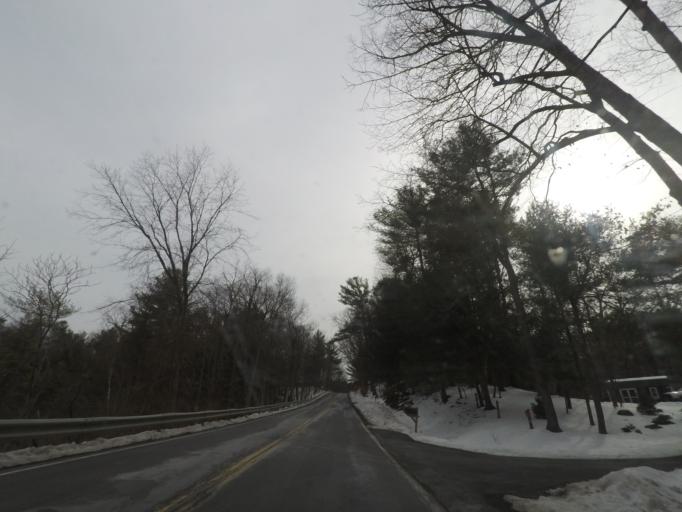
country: US
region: New York
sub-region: Albany County
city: Voorheesville
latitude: 42.6614
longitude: -73.9839
